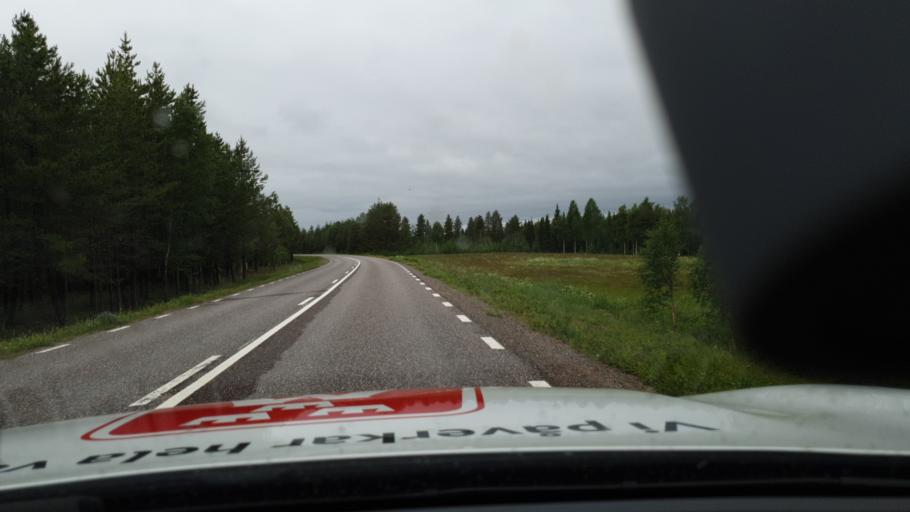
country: SE
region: Norrbotten
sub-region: Pajala Kommun
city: Pajala
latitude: 67.1939
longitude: 23.4640
